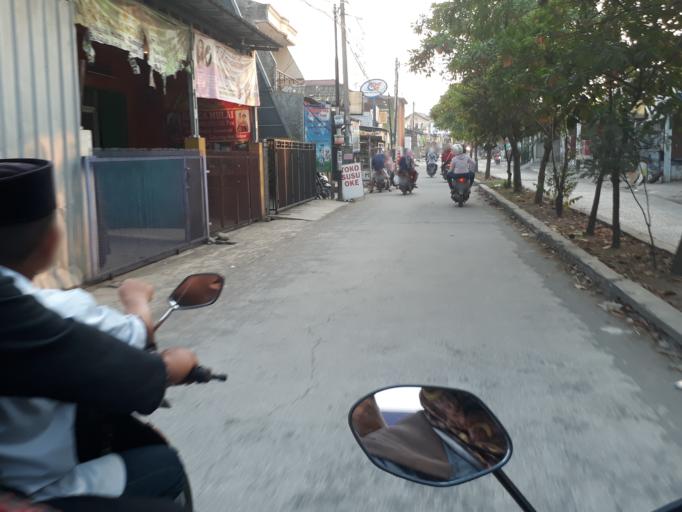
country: ID
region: West Java
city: Bekasi
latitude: -6.2435
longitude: 107.0476
